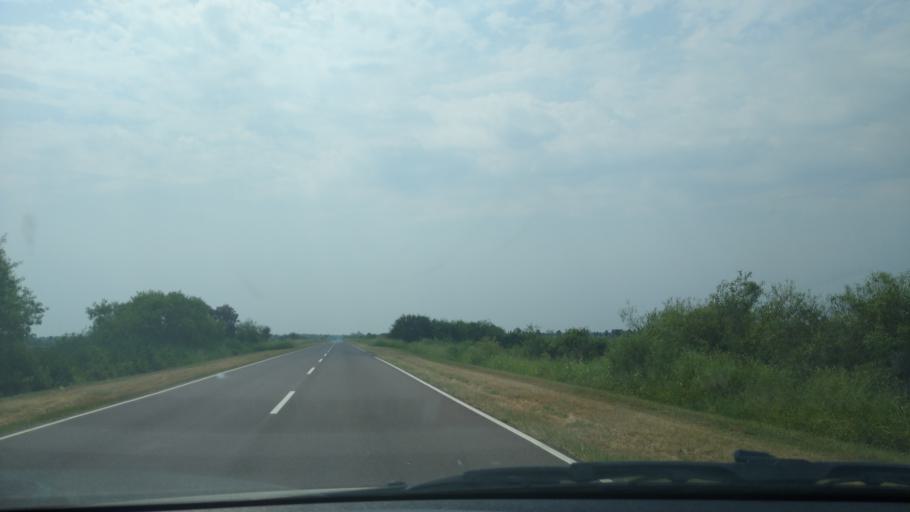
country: AR
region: Chaco
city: La Eduvigis
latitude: -26.9925
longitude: -58.9742
